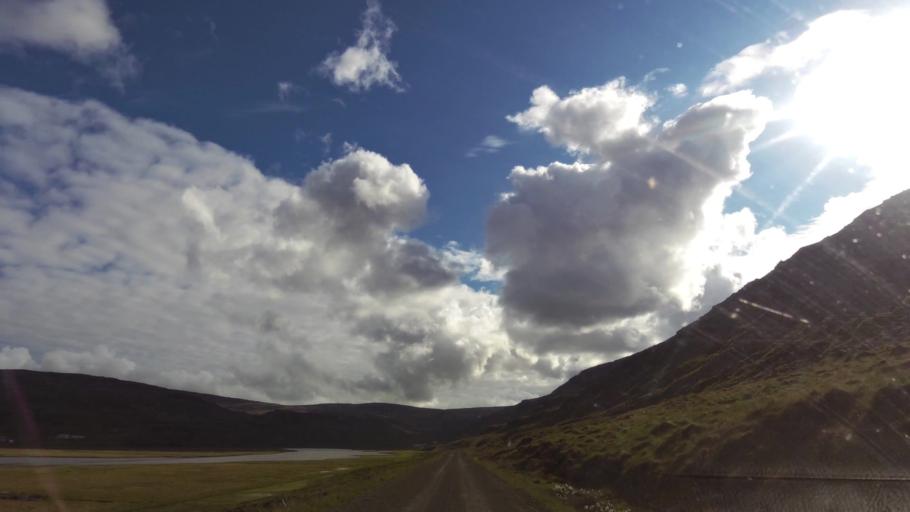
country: IS
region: West
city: Olafsvik
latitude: 65.5748
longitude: -24.1557
